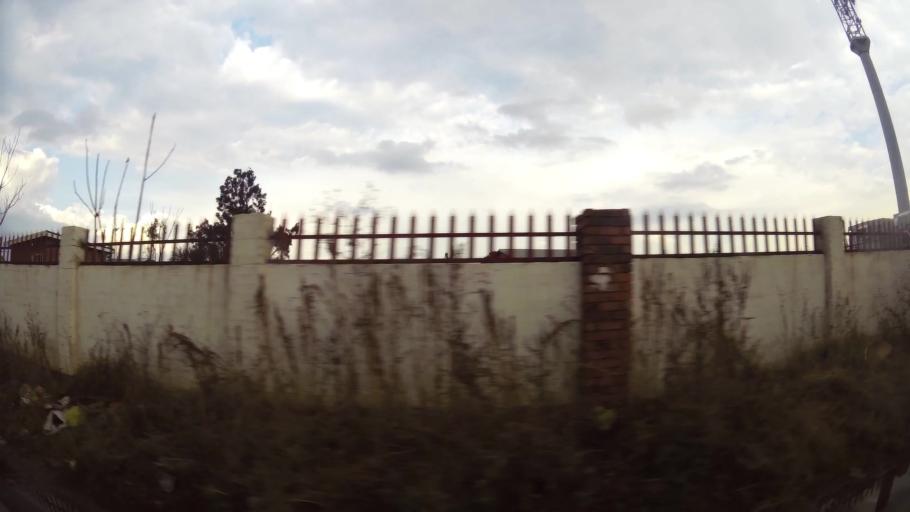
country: ZA
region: Gauteng
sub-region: Ekurhuleni Metropolitan Municipality
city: Germiston
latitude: -26.3677
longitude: 28.1267
